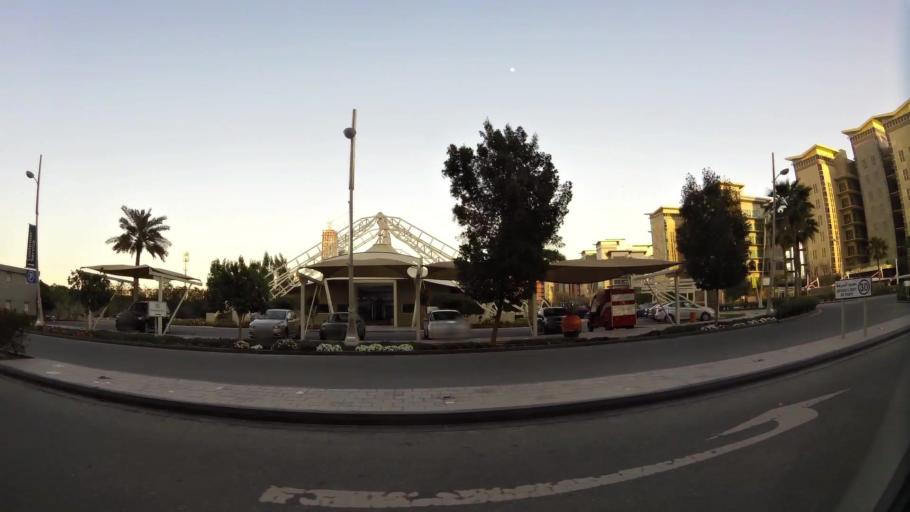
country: BH
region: Manama
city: Jidd Hafs
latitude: 26.2372
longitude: 50.5632
